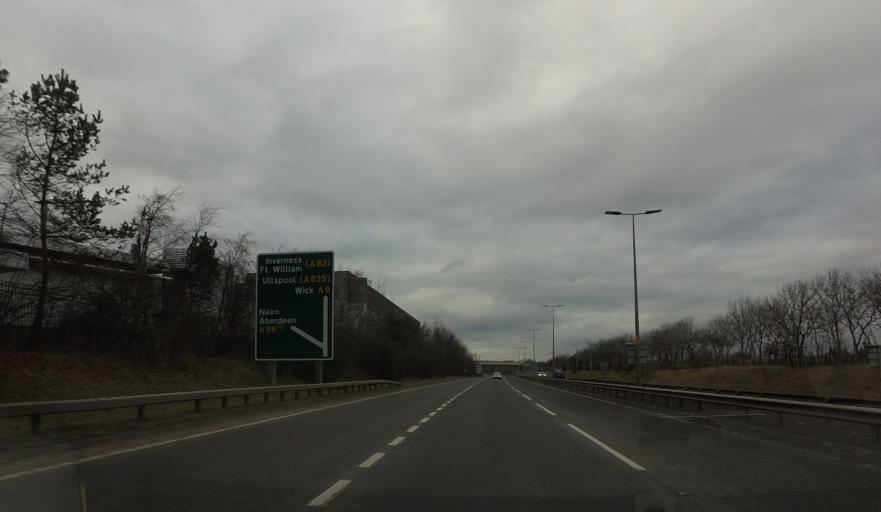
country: GB
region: Scotland
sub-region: Highland
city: Inverness
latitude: 57.4762
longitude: -4.1878
